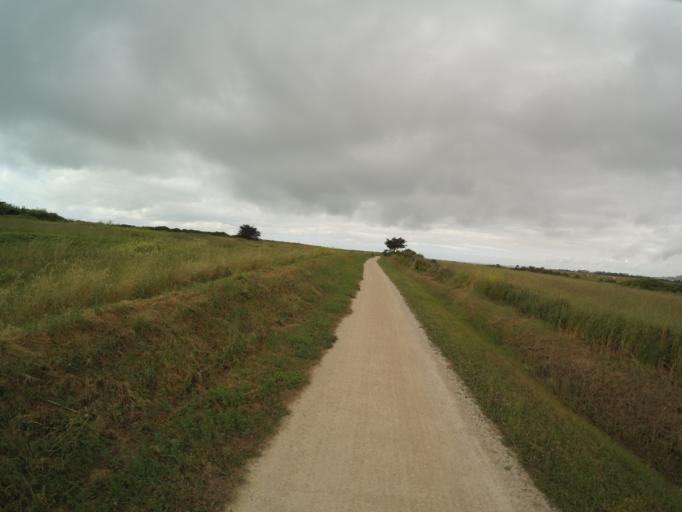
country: FR
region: Poitou-Charentes
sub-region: Departement de la Charente-Maritime
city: Aytre
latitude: 46.1310
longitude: -1.1453
